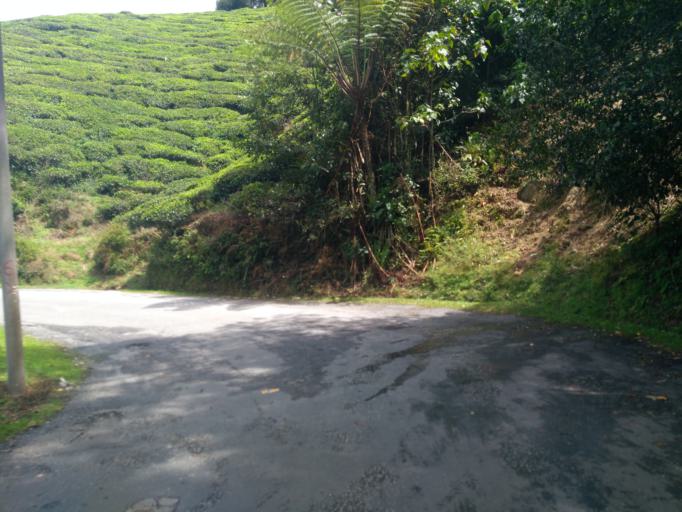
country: MY
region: Pahang
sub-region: Cameron Highlands
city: Tanah Rata
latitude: 4.5190
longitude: 101.4088
